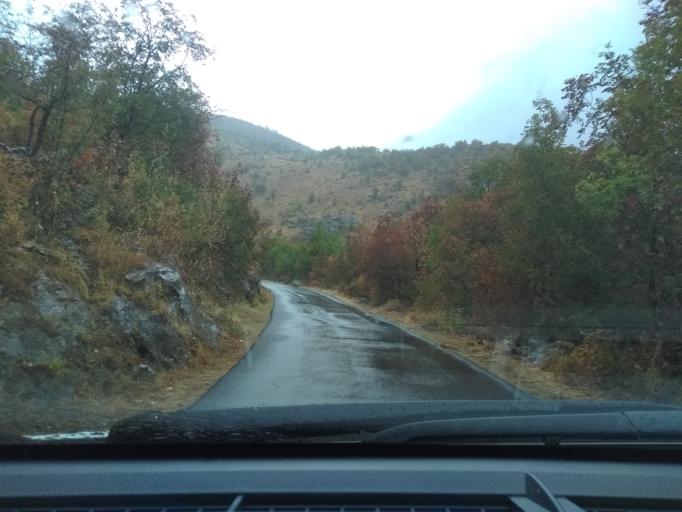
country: ME
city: Stari Bar
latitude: 42.1817
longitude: 19.1760
